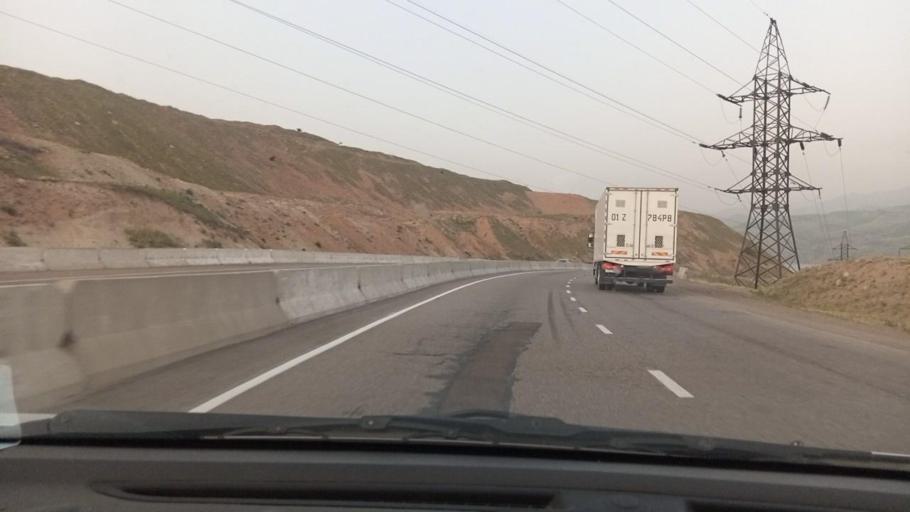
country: UZ
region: Toshkent
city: Angren
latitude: 41.0601
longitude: 70.1902
